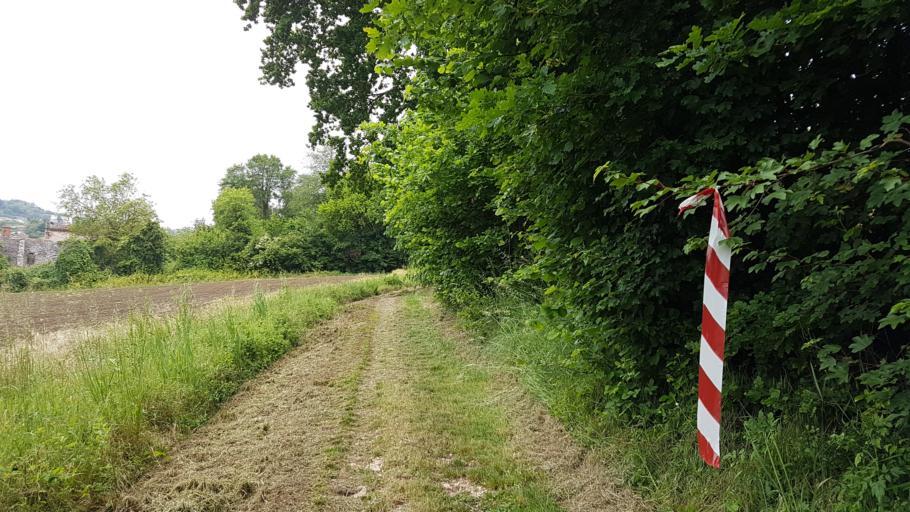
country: IT
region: Veneto
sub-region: Provincia di Vicenza
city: Tezze
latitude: 45.5486
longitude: 11.3416
